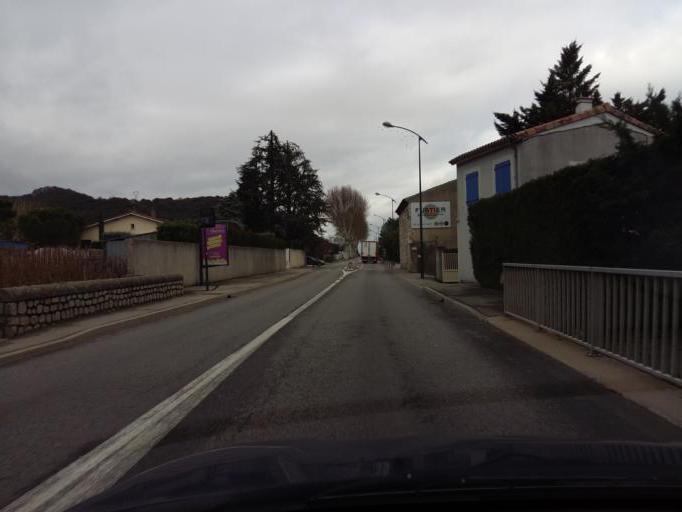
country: FR
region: Rhone-Alpes
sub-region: Departement de l'Ardeche
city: Cornas
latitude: 44.9645
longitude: 4.8491
